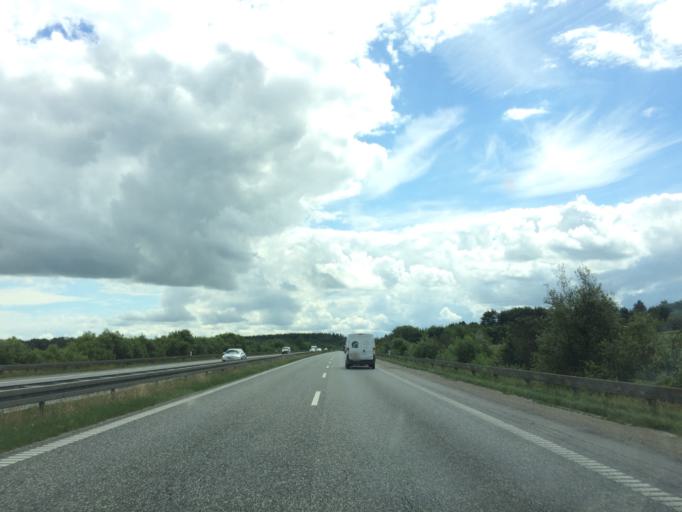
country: DK
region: North Denmark
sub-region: Mariagerfjord Kommune
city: Hobro
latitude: 56.6494
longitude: 9.7379
